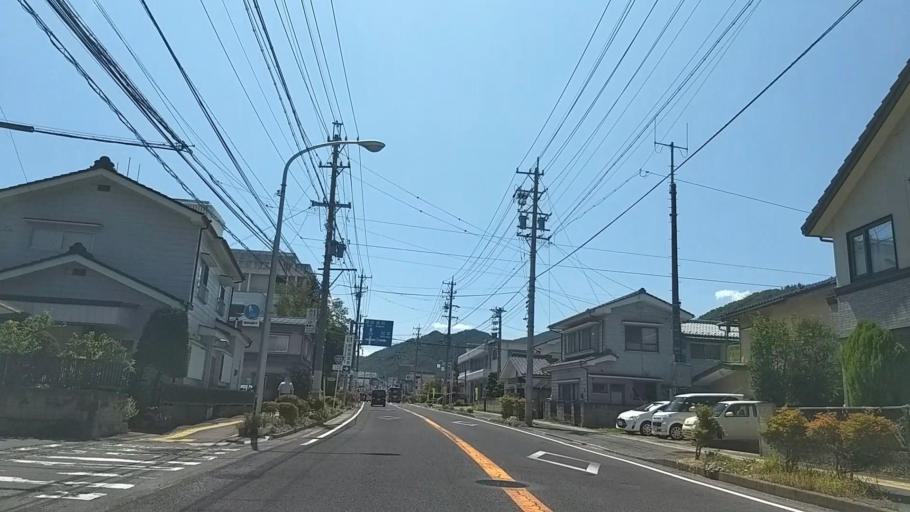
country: JP
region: Nagano
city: Kamimaruko
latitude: 36.3248
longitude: 138.2698
